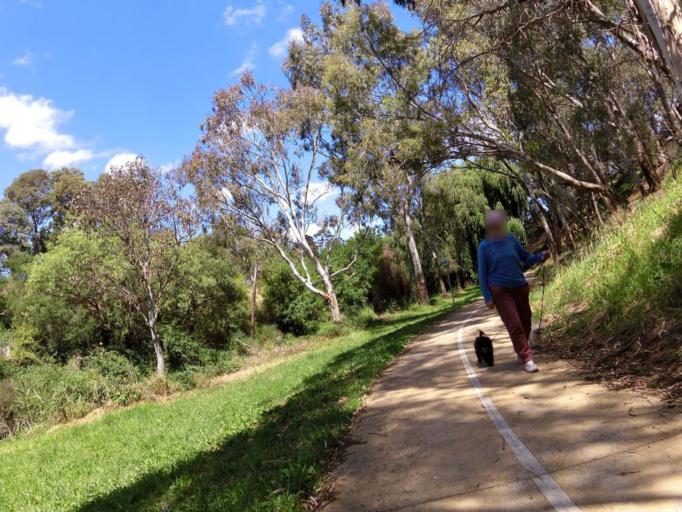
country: AU
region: Victoria
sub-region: Moreland
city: Fawkner
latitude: -37.7235
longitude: 144.9686
